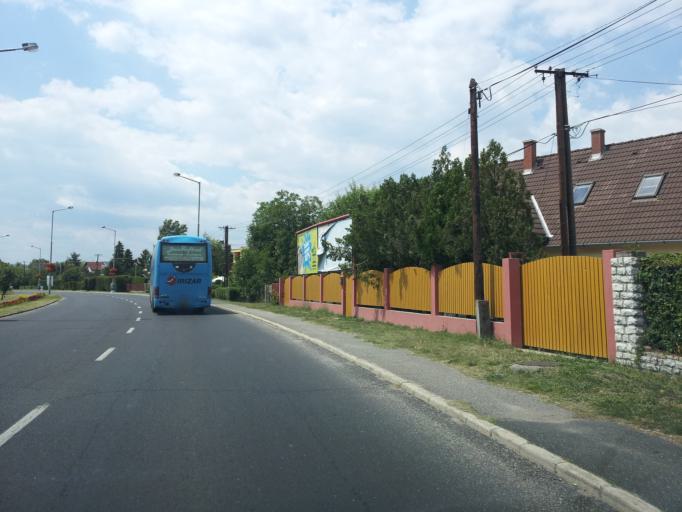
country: HU
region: Veszprem
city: Csopak
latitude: 46.9857
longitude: 17.9753
